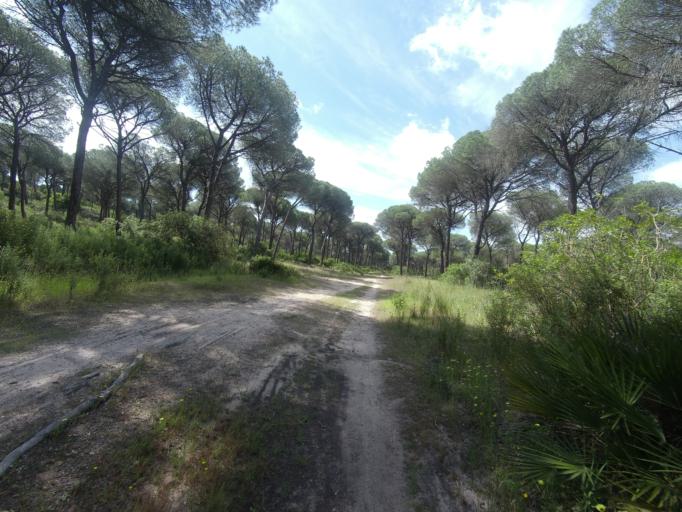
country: ES
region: Andalusia
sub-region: Provincia de Huelva
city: Aljaraque
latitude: 37.2276
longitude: -7.0673
